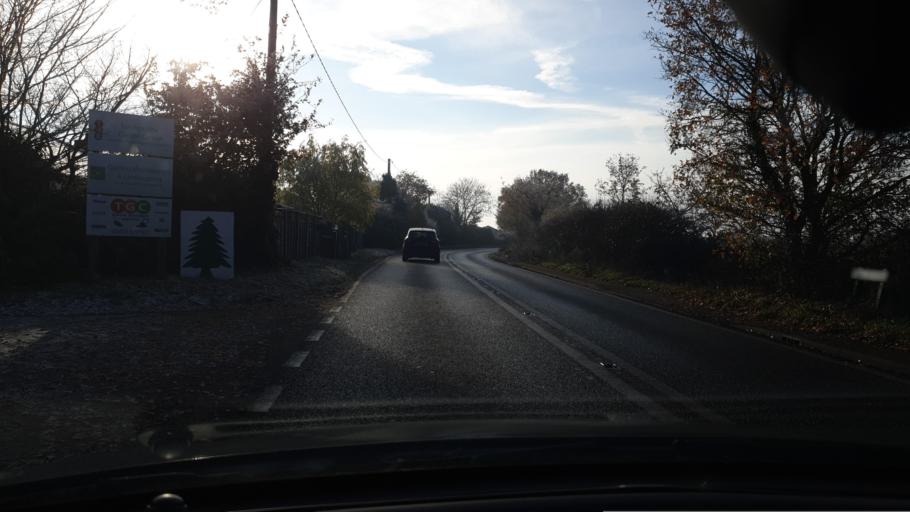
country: GB
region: England
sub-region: Essex
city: Mistley
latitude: 51.9843
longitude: 1.0973
